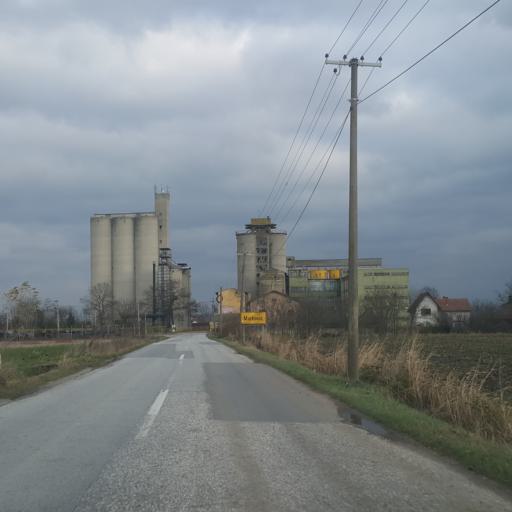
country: RS
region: Central Serbia
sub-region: Sumadijski Okrug
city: Lapovo
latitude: 44.2359
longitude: 21.0924
